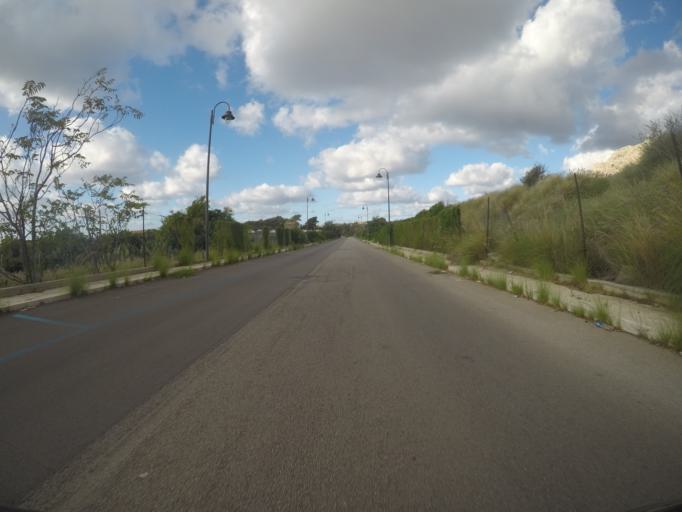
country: IT
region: Sicily
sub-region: Palermo
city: Isola delle Femmine
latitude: 38.1906
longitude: 13.2452
